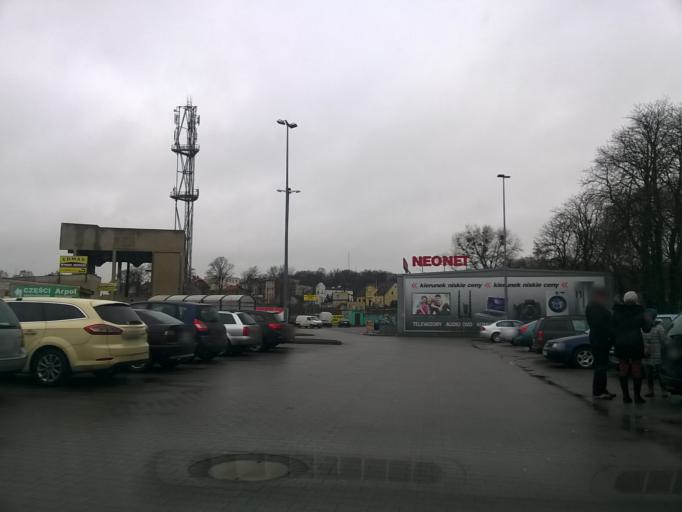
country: PL
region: Kujawsko-Pomorskie
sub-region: Powiat nakielski
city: Naklo nad Notecia
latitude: 53.1371
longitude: 17.5904
